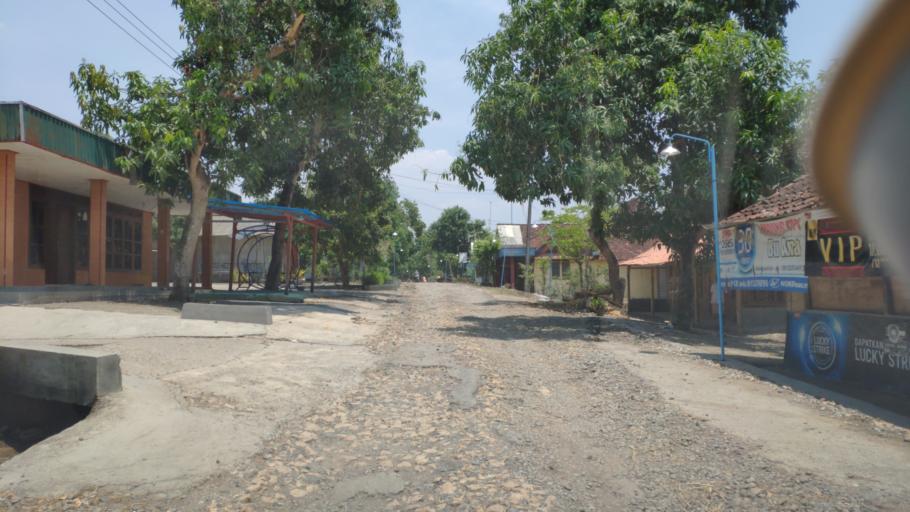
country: ID
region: Central Java
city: Karangtengah
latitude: -7.0420
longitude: 111.3128
